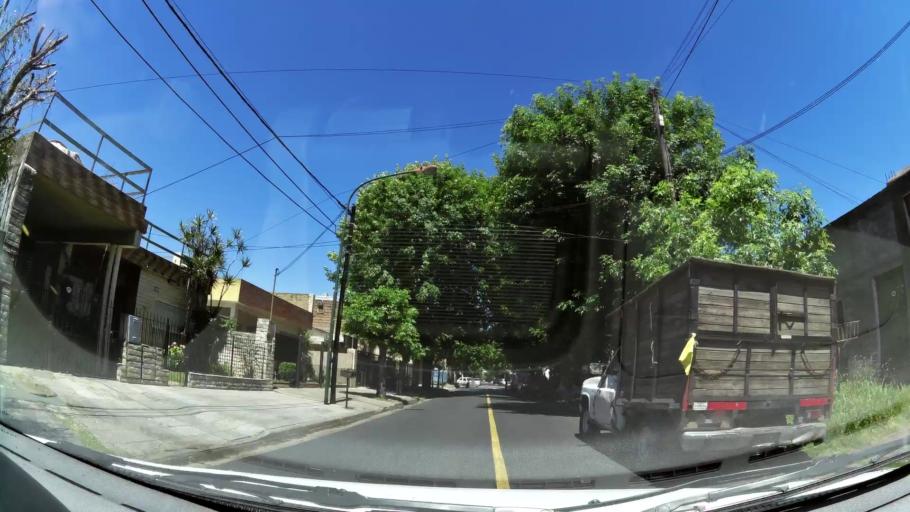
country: AR
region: Buenos Aires
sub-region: Partido de San Isidro
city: San Isidro
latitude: -34.5101
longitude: -58.5563
